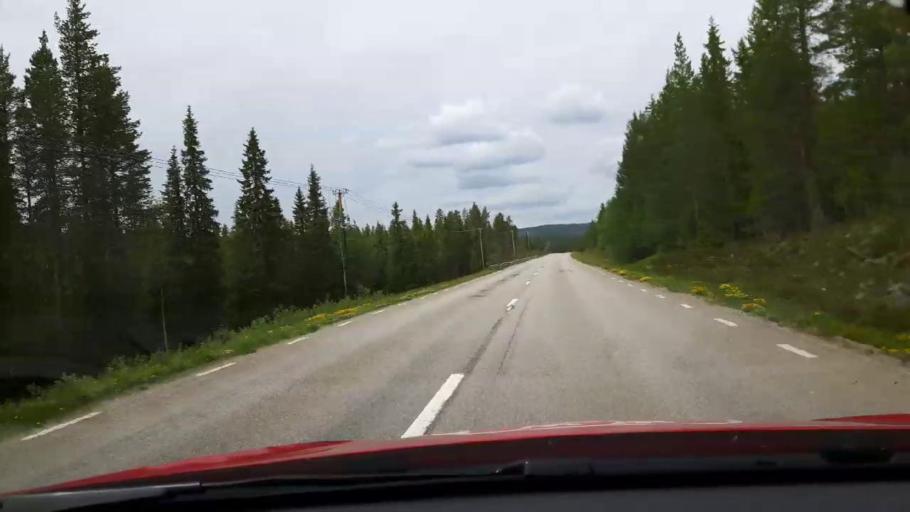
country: SE
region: Jaemtland
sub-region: Harjedalens Kommun
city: Sveg
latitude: 62.3987
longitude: 13.7458
